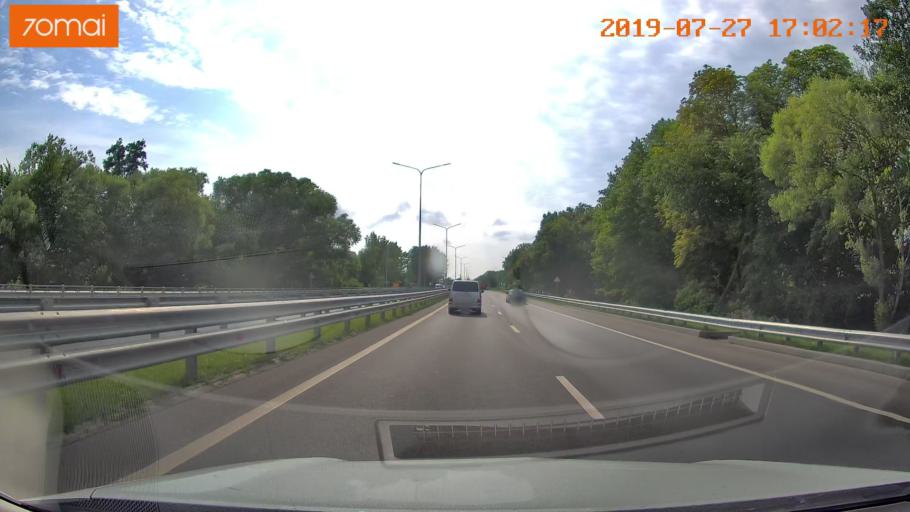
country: RU
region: Kaliningrad
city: Bol'shoe Isakovo
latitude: 54.7071
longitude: 20.6212
